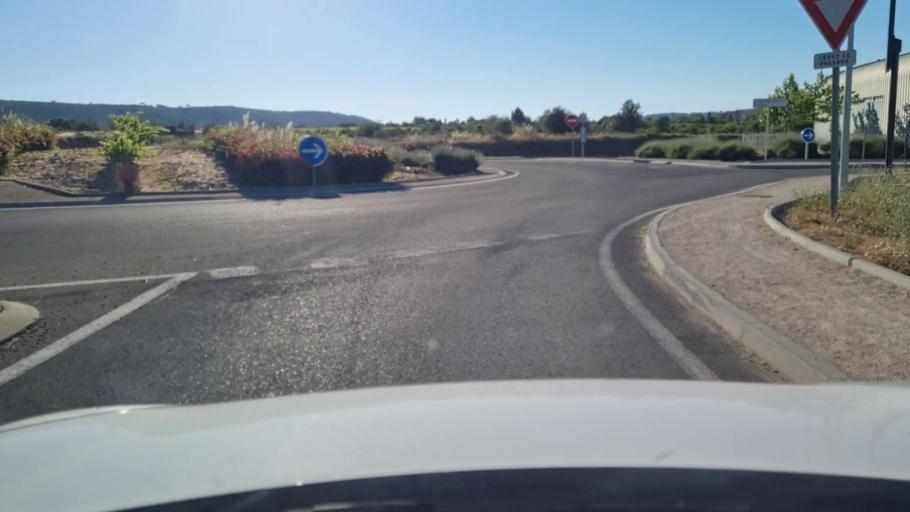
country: FR
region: Languedoc-Roussillon
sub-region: Departement du Gard
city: Clarensac
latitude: 43.8281
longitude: 4.2304
